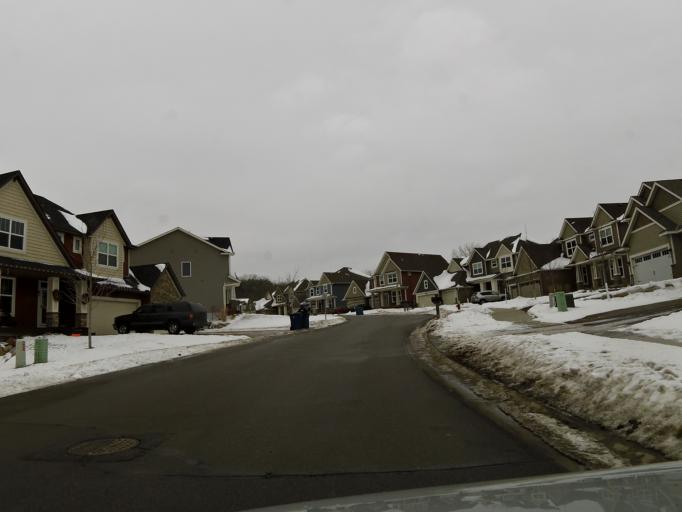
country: US
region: Minnesota
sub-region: Dakota County
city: Inver Grove Heights
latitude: 44.8408
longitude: -93.0864
